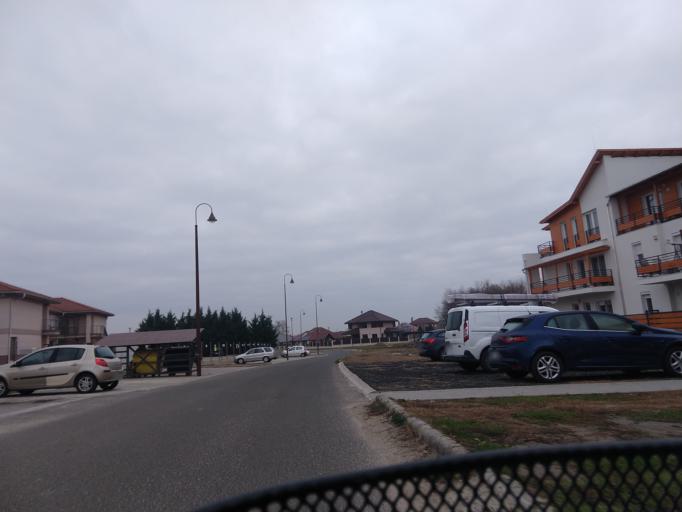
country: HU
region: Pest
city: Orbottyan
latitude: 47.6588
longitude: 19.2565
